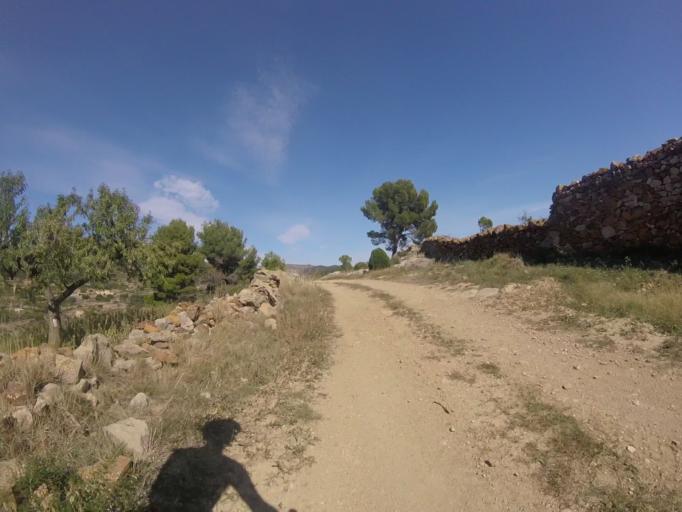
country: ES
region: Valencia
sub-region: Provincia de Castello
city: Sierra-Engarceran
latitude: 40.2741
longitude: 0.0037
